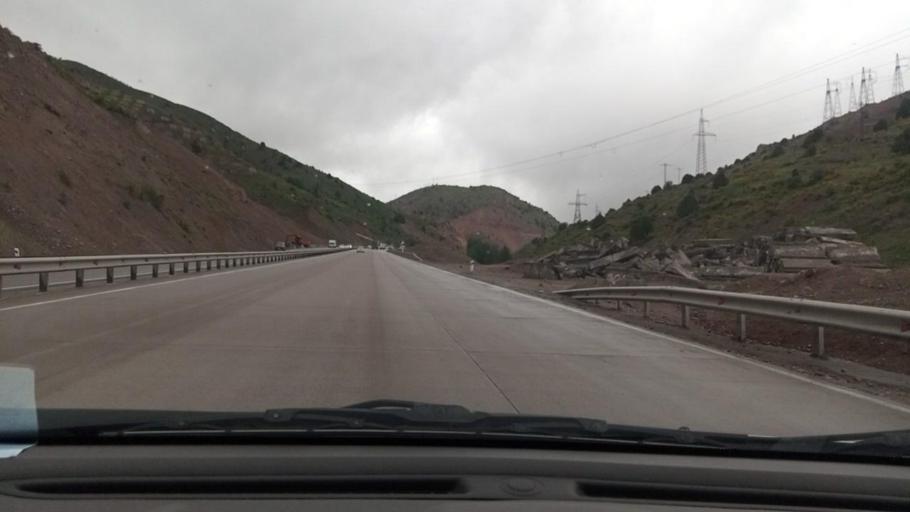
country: UZ
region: Toshkent
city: Angren
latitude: 41.0571
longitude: 70.5634
